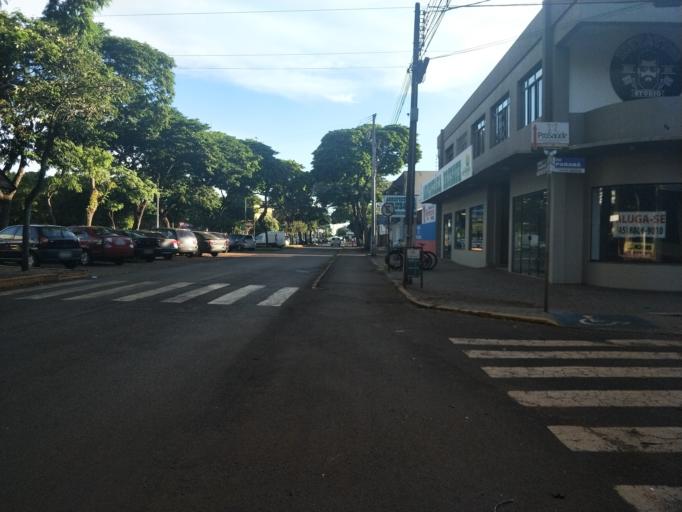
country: BR
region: Parana
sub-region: Marechal Candido Rondon
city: Marechal Candido Rondon
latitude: -24.5618
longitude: -54.0585
